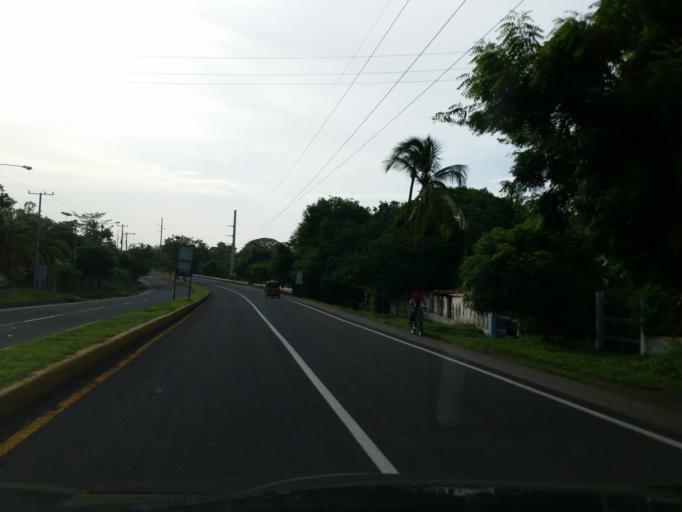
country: NI
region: Granada
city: Granada
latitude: 11.9684
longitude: -86.0152
